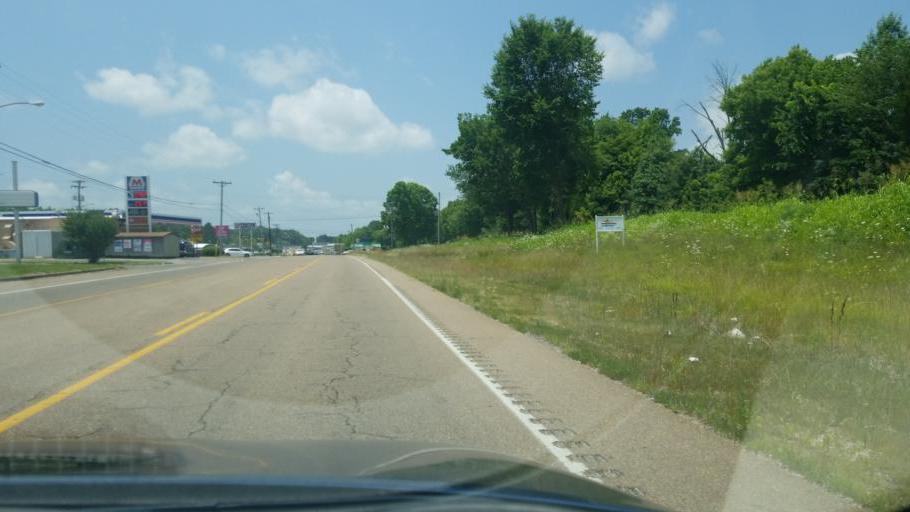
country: US
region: Tennessee
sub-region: Carroll County
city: Huntingdon
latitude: 36.0079
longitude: -88.4048
